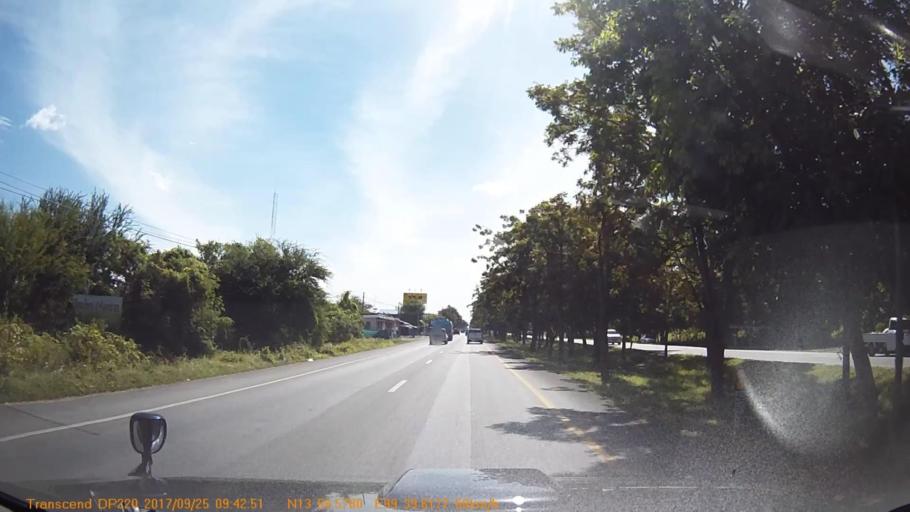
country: TH
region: Kanchanaburi
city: Tha Muang
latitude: 13.9762
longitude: 99.6607
